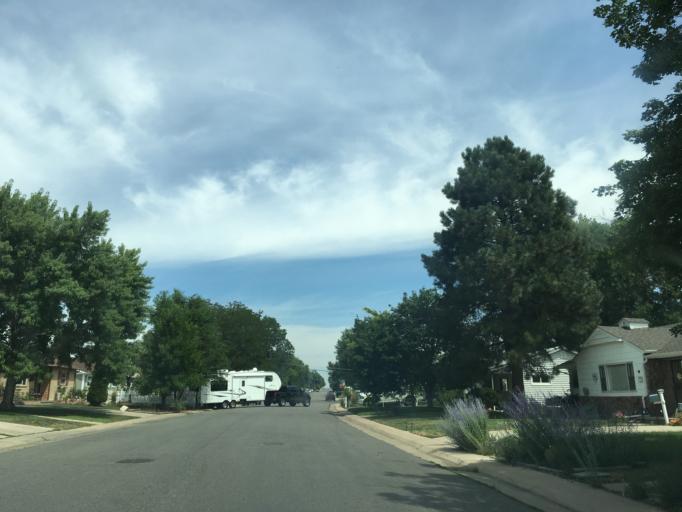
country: US
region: Colorado
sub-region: Jefferson County
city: Lakewood
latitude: 39.6921
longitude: -105.0401
